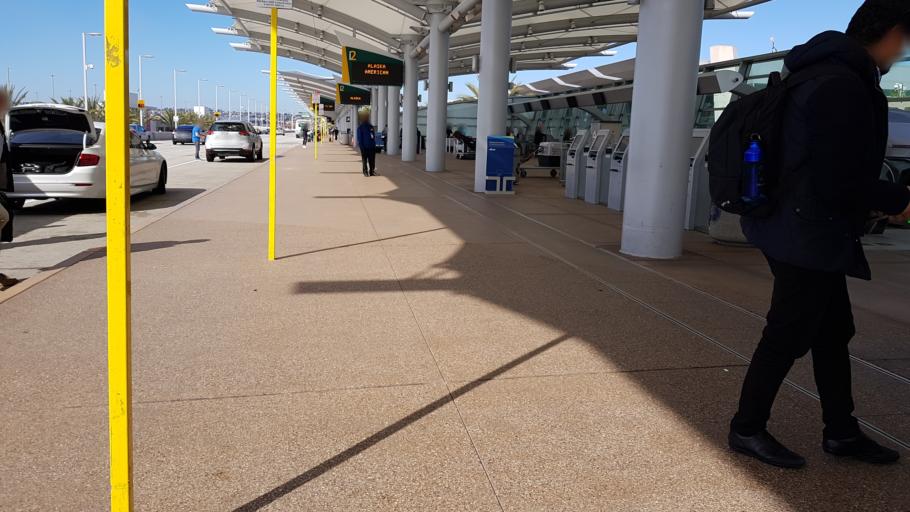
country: US
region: California
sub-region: San Diego County
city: San Diego
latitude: 32.7312
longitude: -117.2011
